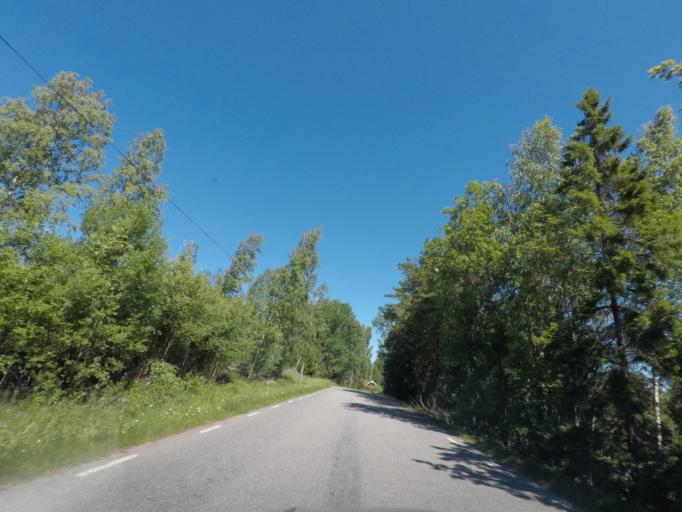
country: SE
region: Uppsala
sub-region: Enkopings Kommun
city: Irsta
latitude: 59.6735
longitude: 16.9032
